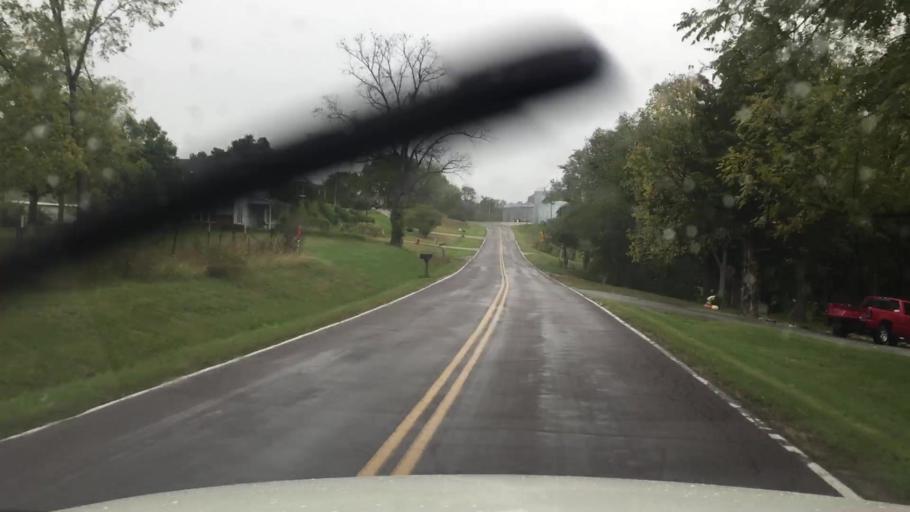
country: US
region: Missouri
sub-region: Boone County
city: Ashland
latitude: 38.7064
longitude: -92.2896
